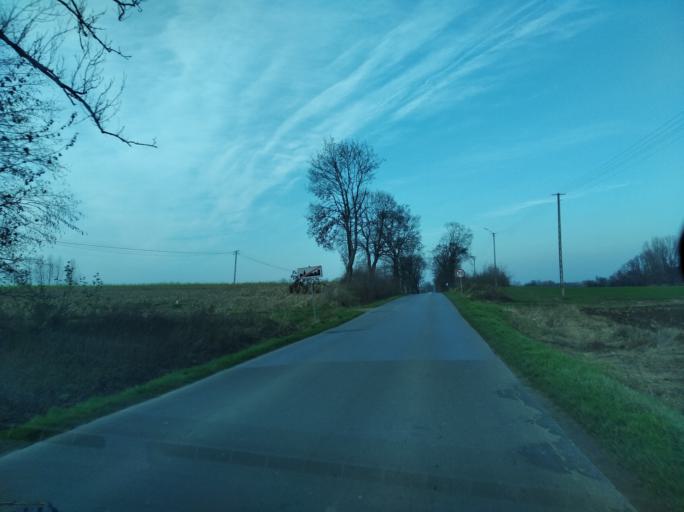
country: PL
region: Subcarpathian Voivodeship
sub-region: Powiat ropczycko-sedziszowski
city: Iwierzyce
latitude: 50.0370
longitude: 21.7463
